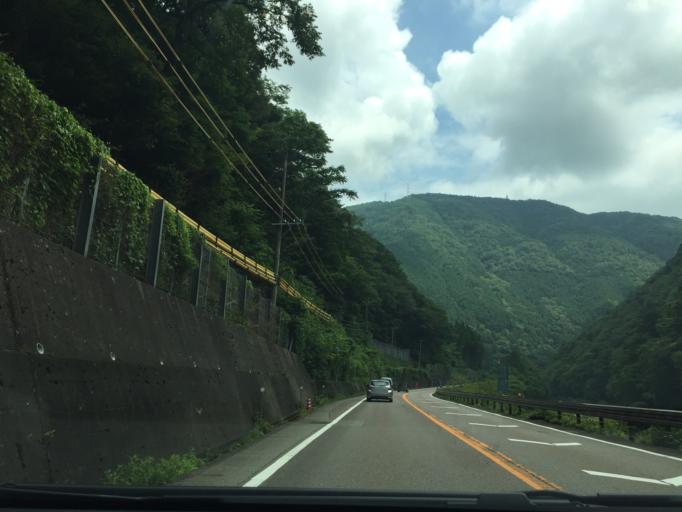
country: JP
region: Gifu
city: Gujo
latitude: 35.7786
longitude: 137.2227
